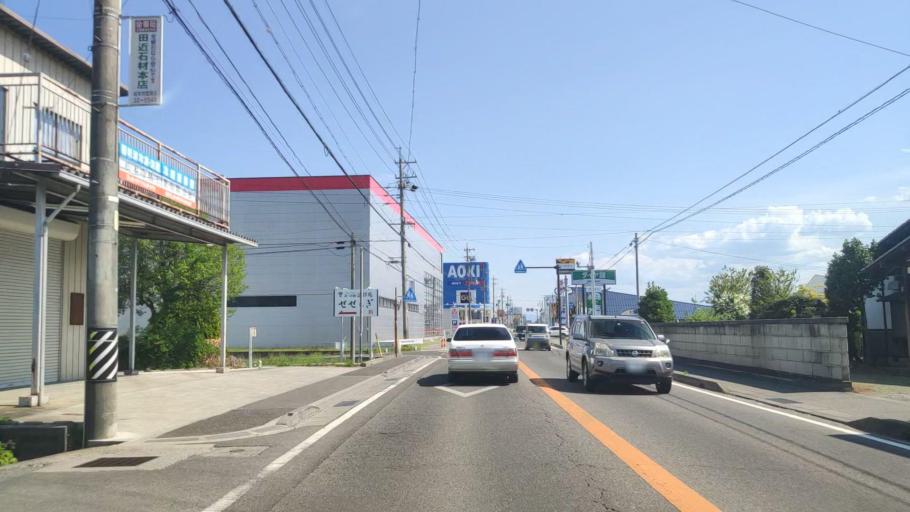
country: JP
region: Nagano
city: Hotaka
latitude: 36.3324
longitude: 137.8912
